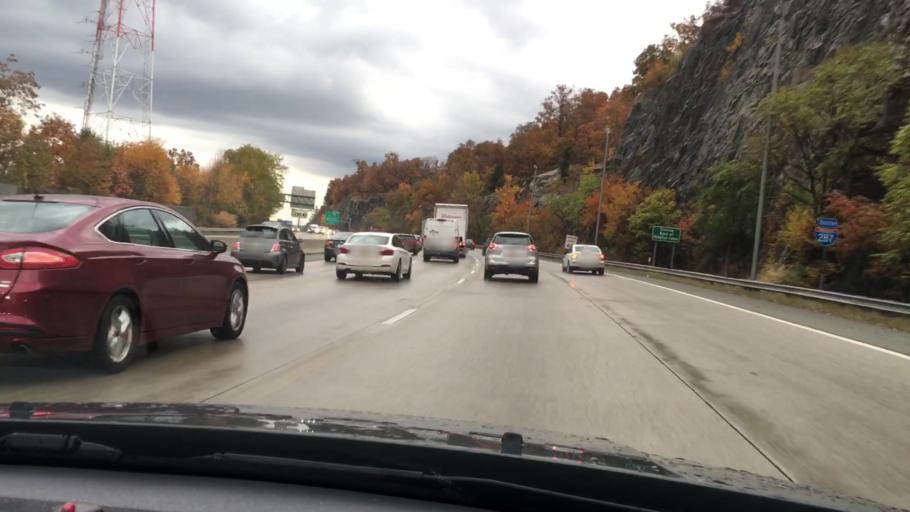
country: US
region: New Jersey
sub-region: Passaic County
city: Pompton Lakes
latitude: 41.0136
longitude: -74.3011
